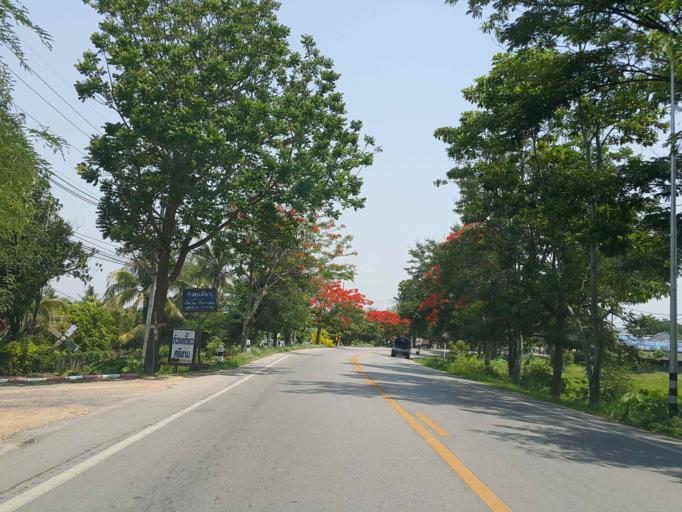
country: TH
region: Chiang Mai
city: Mae Taeng
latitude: 19.0310
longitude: 98.9668
